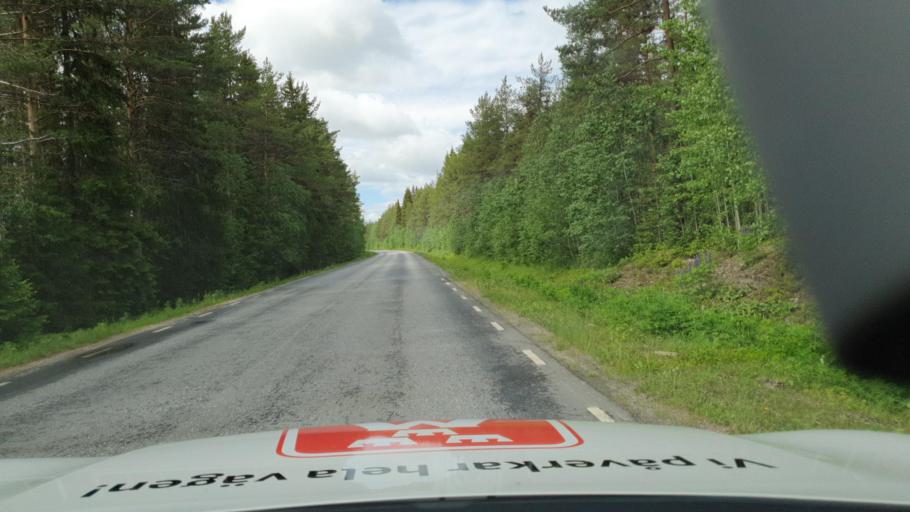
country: SE
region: Vaesterbotten
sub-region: Dorotea Kommun
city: Dorotea
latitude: 64.2619
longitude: 16.3687
